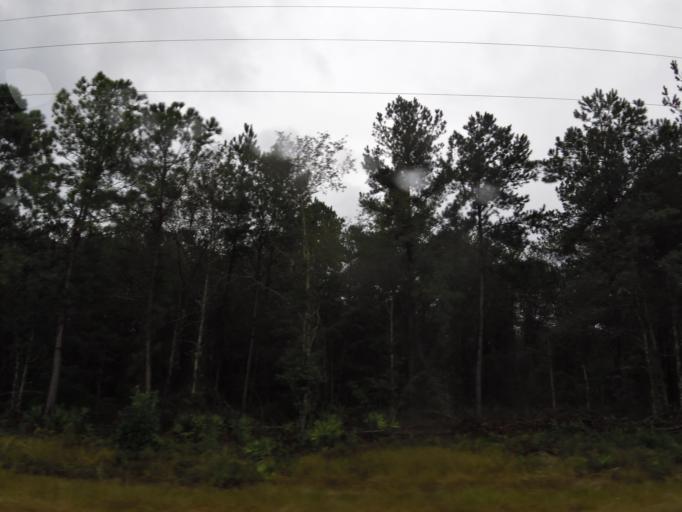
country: US
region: Georgia
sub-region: Wayne County
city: Jesup
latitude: 31.5532
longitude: -81.8162
